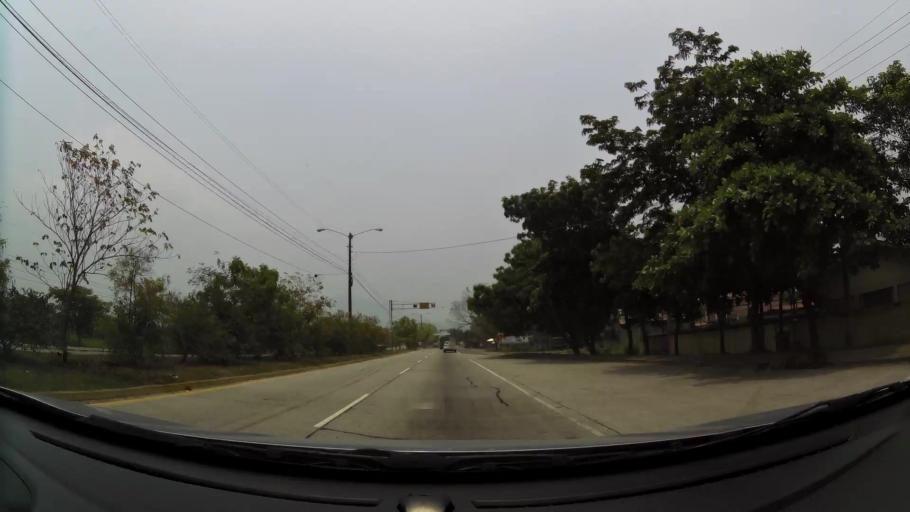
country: HN
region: Yoro
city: El Progreso
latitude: 15.4053
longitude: -87.8247
